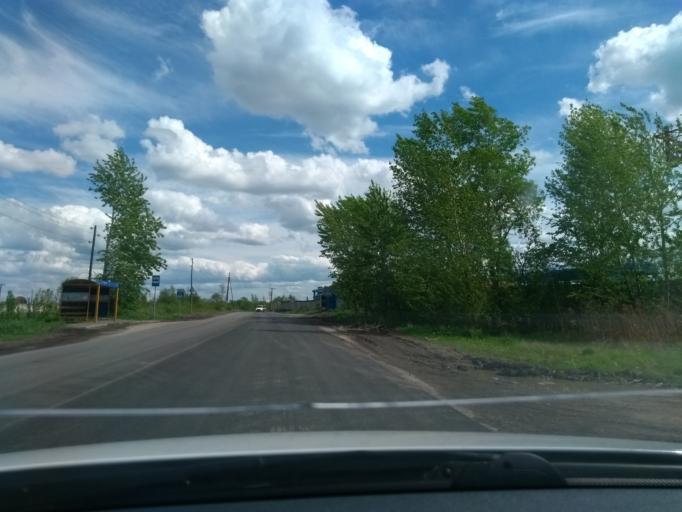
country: RU
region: Perm
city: Kondratovo
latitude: 58.0112
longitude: 56.0728
